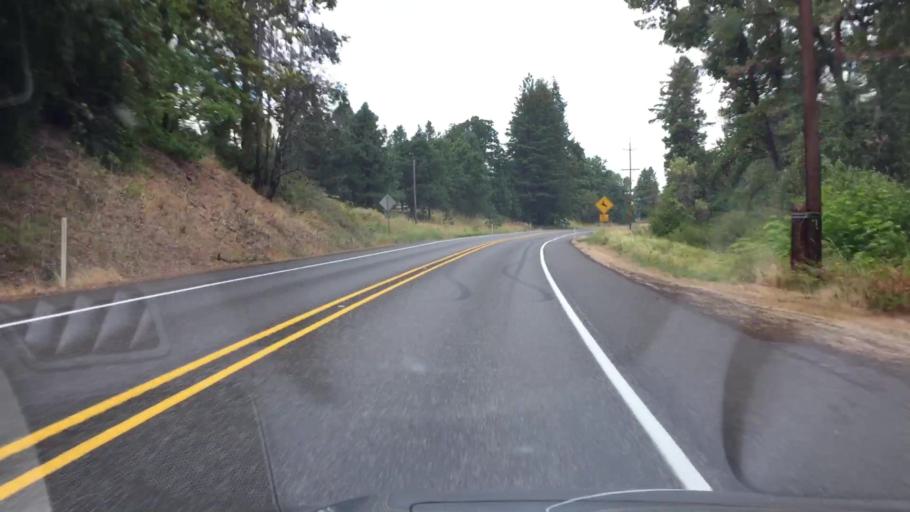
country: US
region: Washington
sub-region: Klickitat County
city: White Salmon
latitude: 45.8059
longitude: -121.4903
